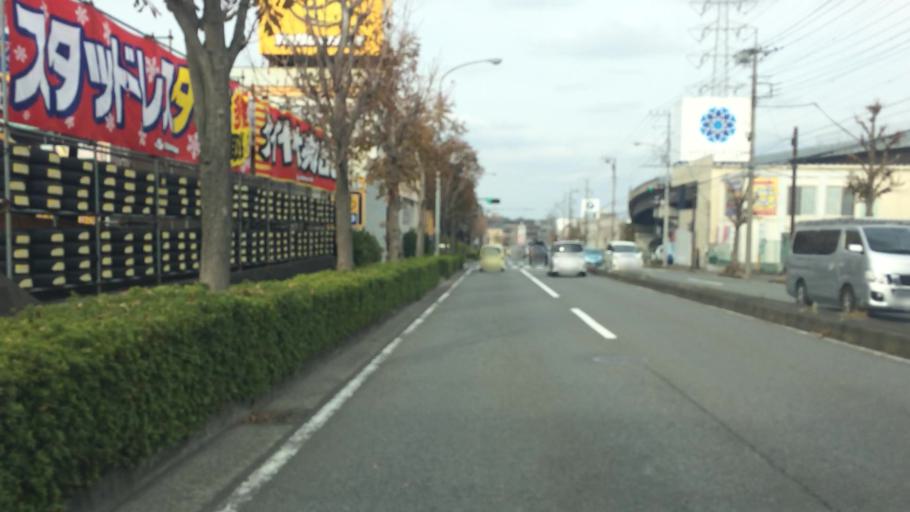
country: JP
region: Kanagawa
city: Yokohama
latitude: 35.5453
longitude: 139.6014
